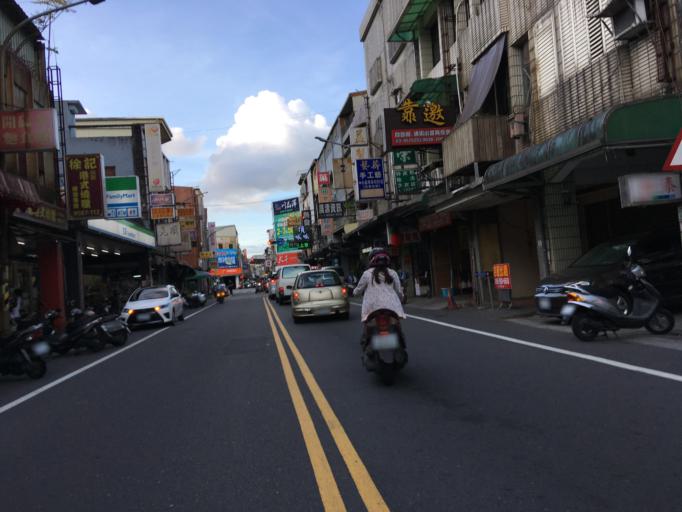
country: TW
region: Taiwan
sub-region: Yilan
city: Yilan
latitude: 24.6671
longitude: 121.7679
